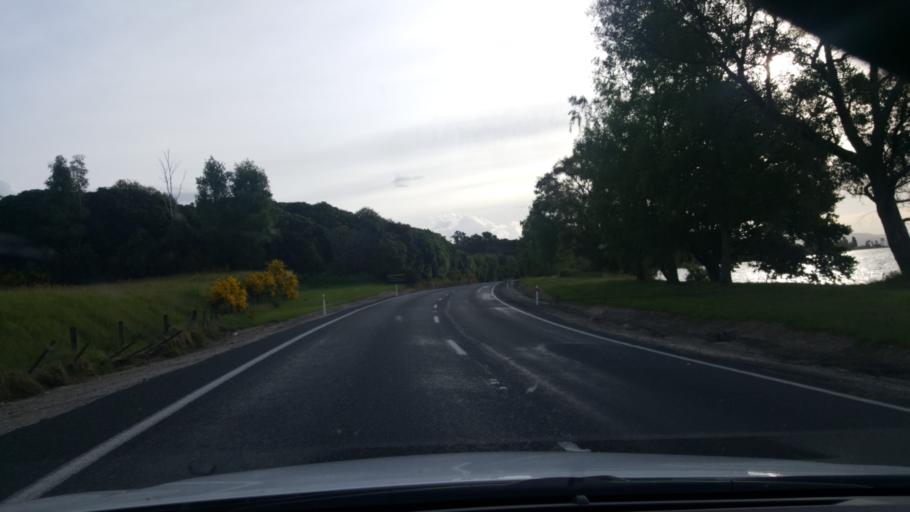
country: NZ
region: Waikato
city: Turangi
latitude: -38.9038
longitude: 175.9414
